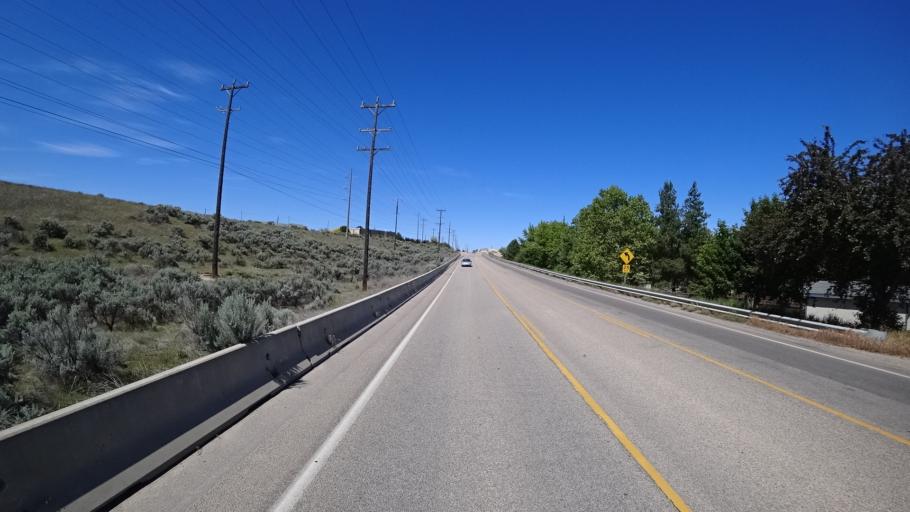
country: US
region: Idaho
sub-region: Ada County
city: Boise
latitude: 43.5606
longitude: -116.1637
